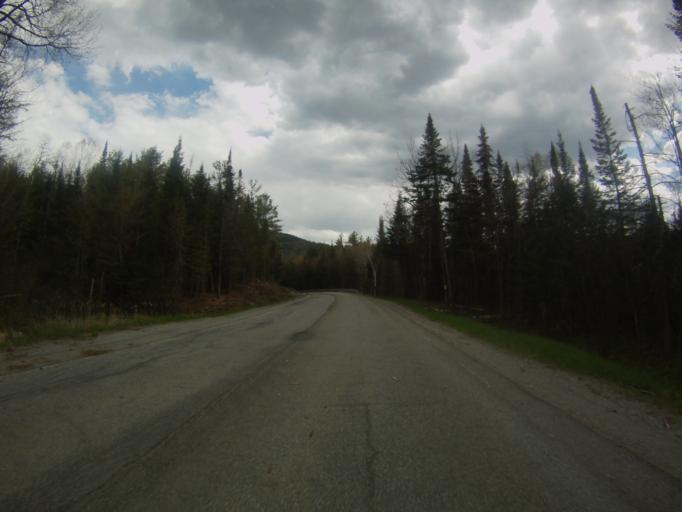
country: US
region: New York
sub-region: Essex County
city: Mineville
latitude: 44.0799
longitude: -73.6096
